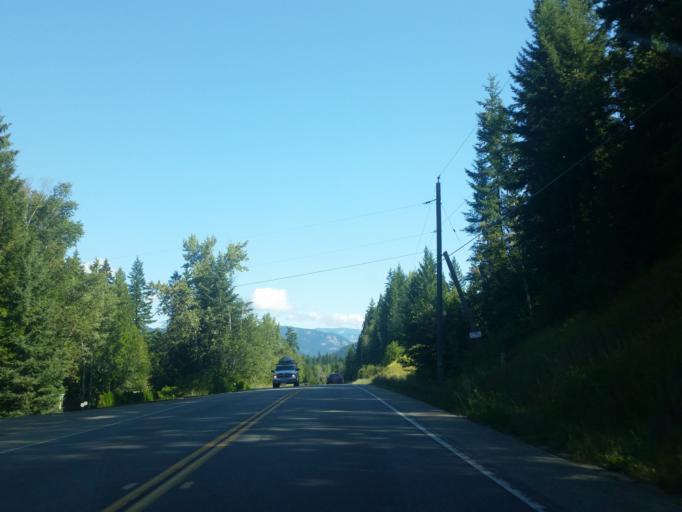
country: CA
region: British Columbia
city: Sicamous
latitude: 50.7106
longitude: -119.0355
